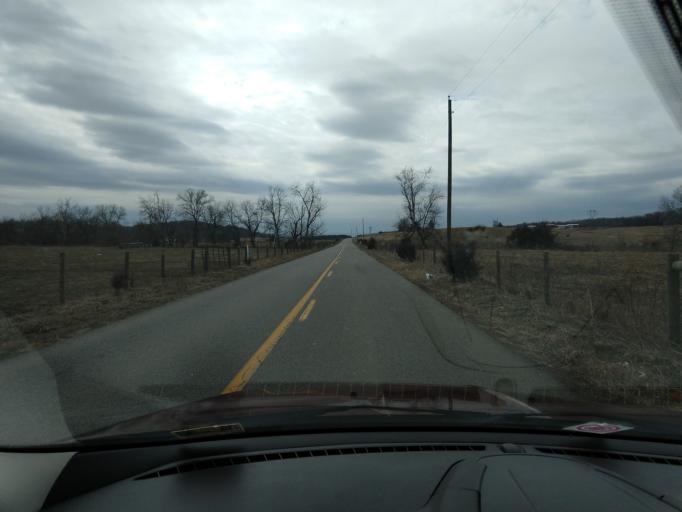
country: US
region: Virginia
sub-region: Augusta County
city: Fishersville
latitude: 38.1559
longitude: -78.9270
